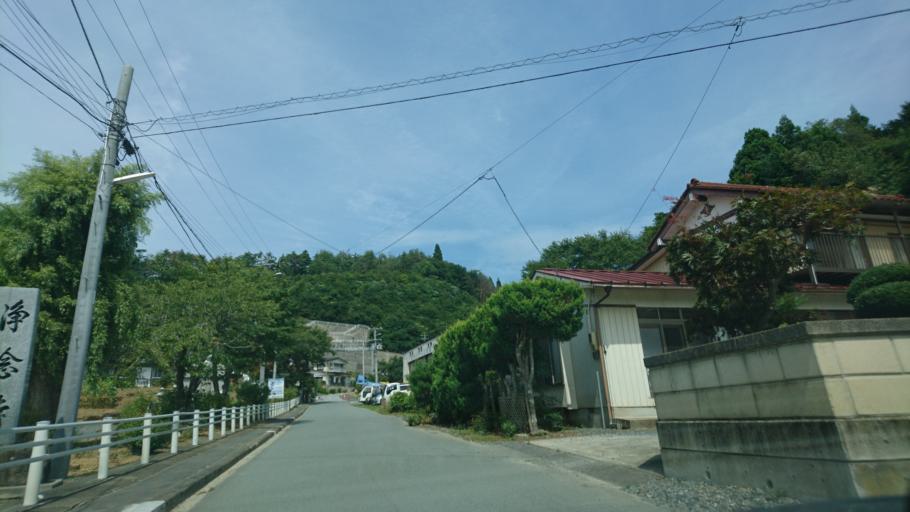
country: JP
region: Iwate
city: Ofunato
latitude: 38.9281
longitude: 141.5860
